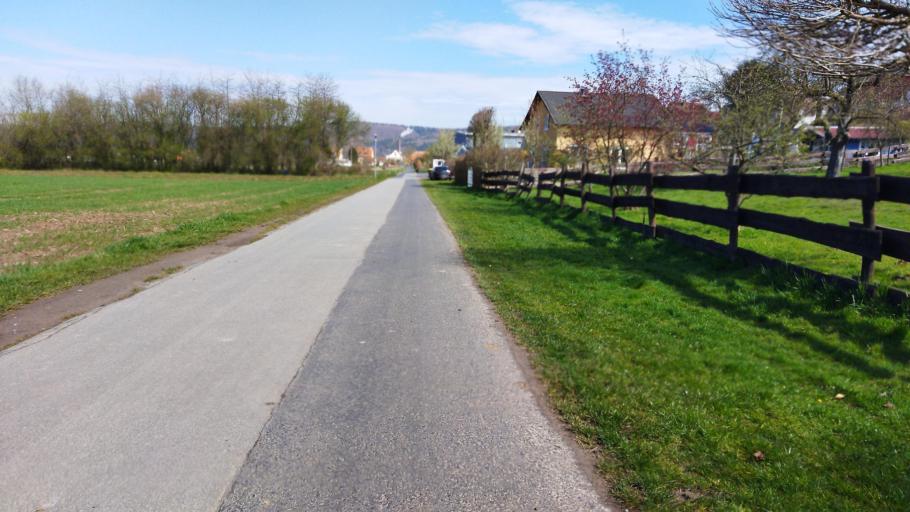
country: DE
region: Lower Saxony
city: Bodenfelde
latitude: 51.6201
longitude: 9.5515
